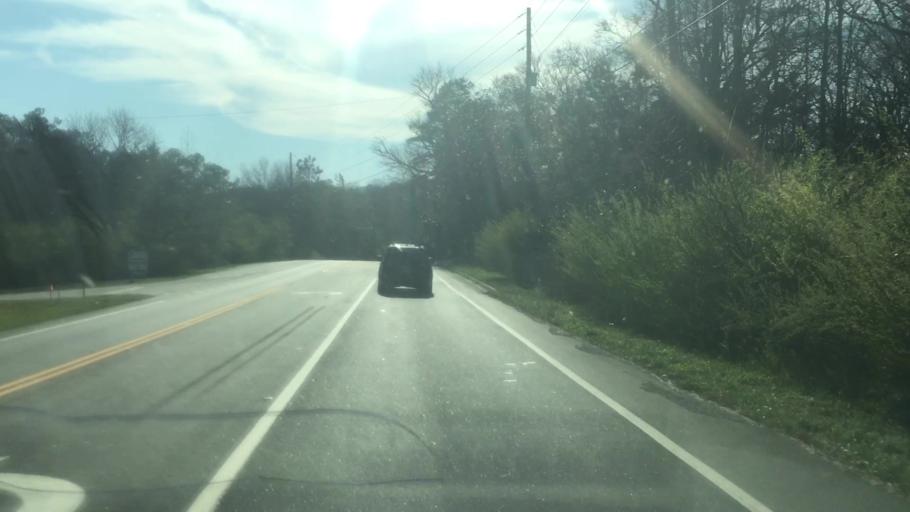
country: US
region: Georgia
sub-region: Cobb County
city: Acworth
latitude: 33.9968
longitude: -84.6886
